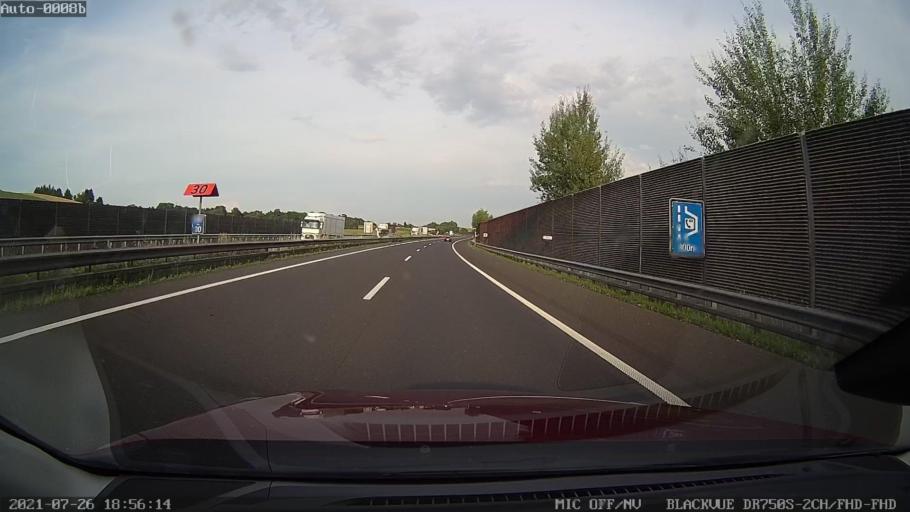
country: AT
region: Upper Austria
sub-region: Wels-Land
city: Offenhausen
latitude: 48.1822
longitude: 13.7958
